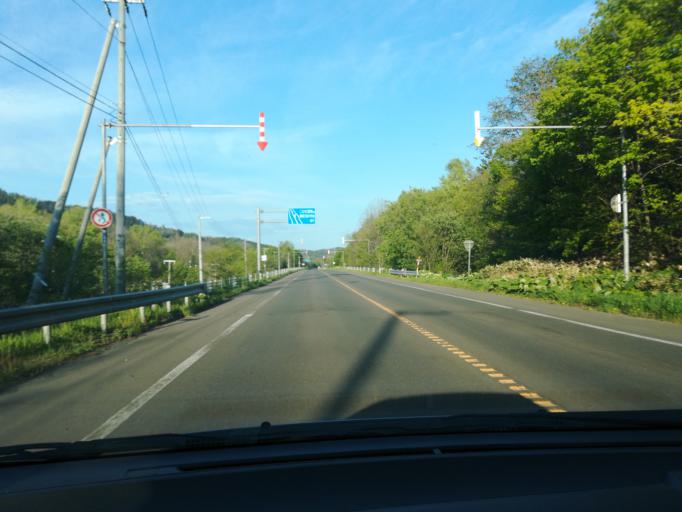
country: JP
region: Hokkaido
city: Shimo-furano
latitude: 43.1390
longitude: 142.6193
